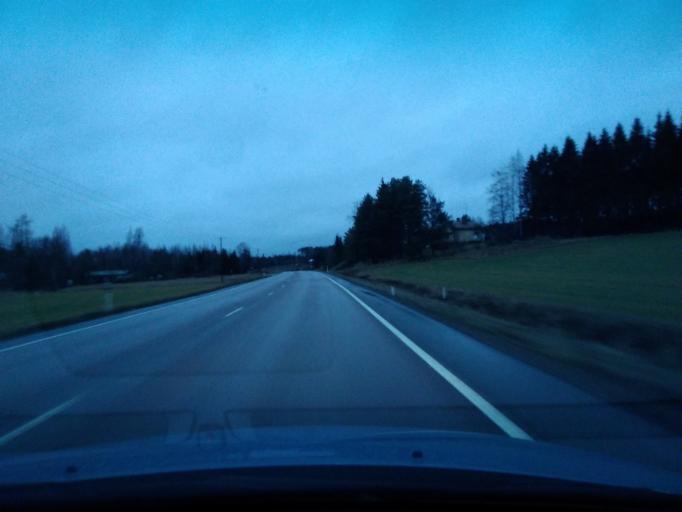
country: FI
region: Uusimaa
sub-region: Porvoo
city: Askola
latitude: 60.4585
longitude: 25.5804
